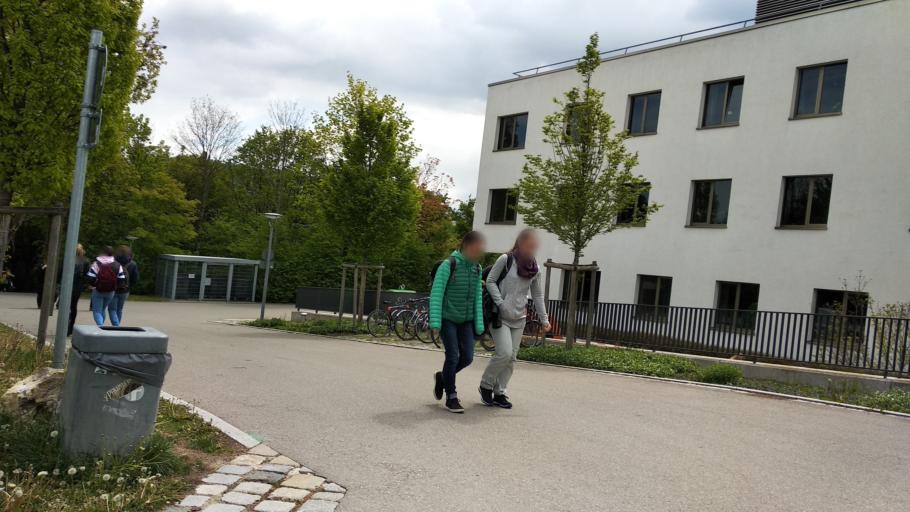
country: DE
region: Bavaria
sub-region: Upper Bavaria
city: Freising
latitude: 48.3995
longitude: 11.7202
